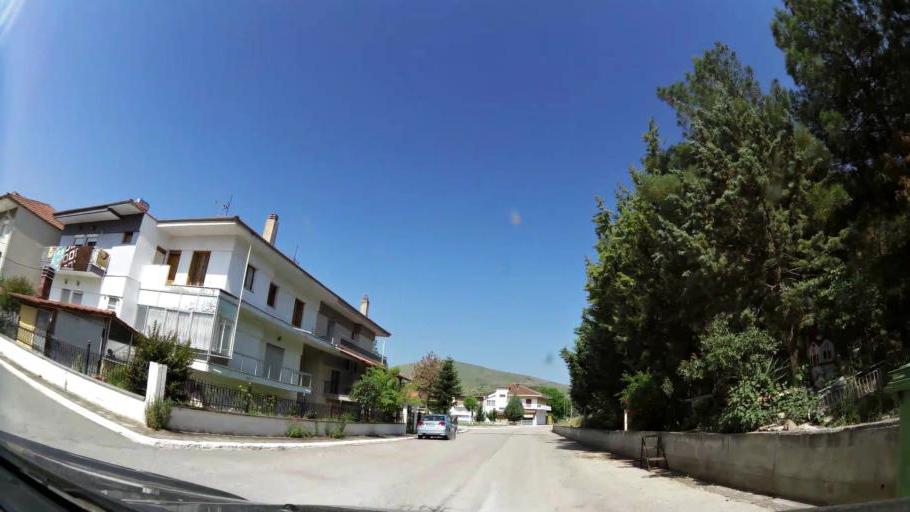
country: GR
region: West Macedonia
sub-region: Nomos Kozanis
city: Koila
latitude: 40.3373
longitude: 21.7900
